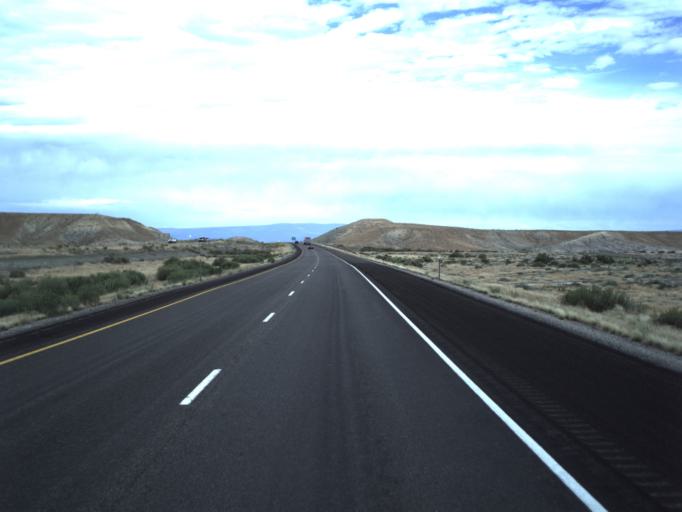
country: US
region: Utah
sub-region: Grand County
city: Moab
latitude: 38.9433
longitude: -109.6396
